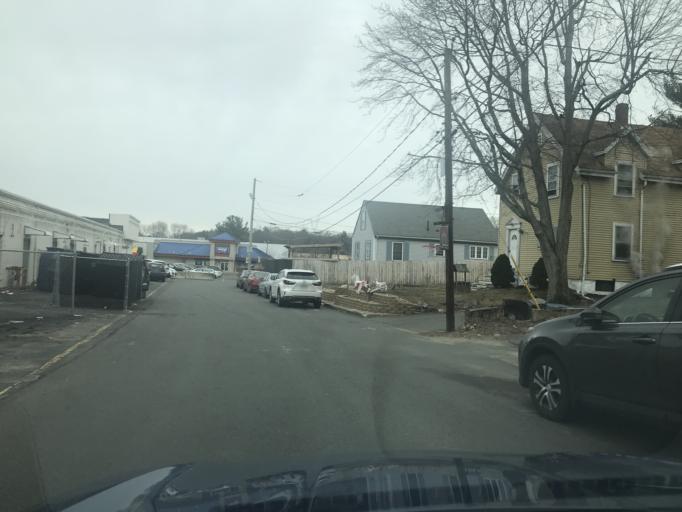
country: US
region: Massachusetts
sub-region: Essex County
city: Saugus
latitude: 42.4929
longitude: -71.0153
